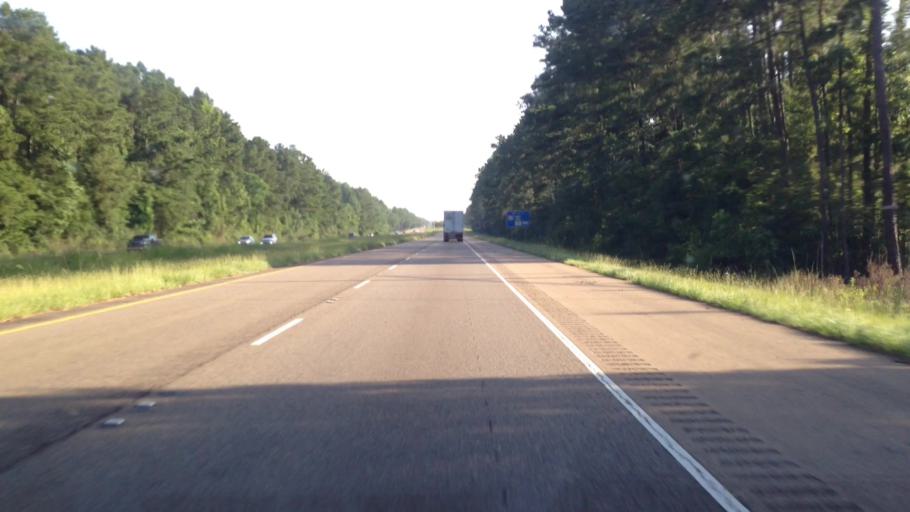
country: US
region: Louisiana
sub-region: Tangipahoa Parish
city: Amite
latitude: 30.7171
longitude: -90.5326
